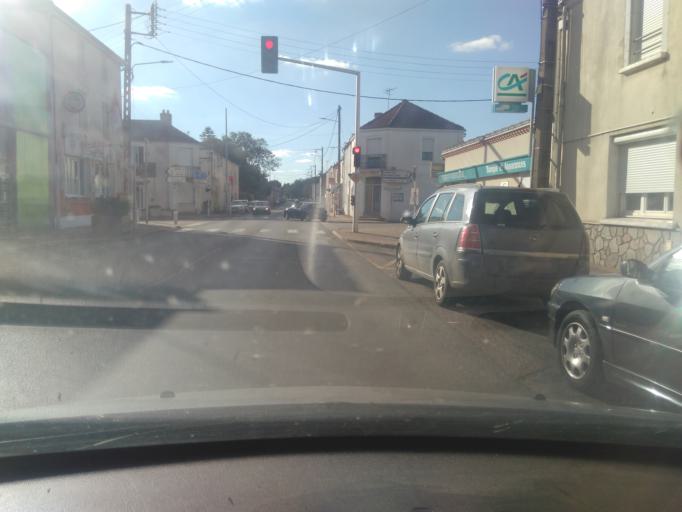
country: FR
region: Pays de la Loire
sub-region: Departement de la Vendee
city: Saint-Florent-des-Bois
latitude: 46.5933
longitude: -1.3154
